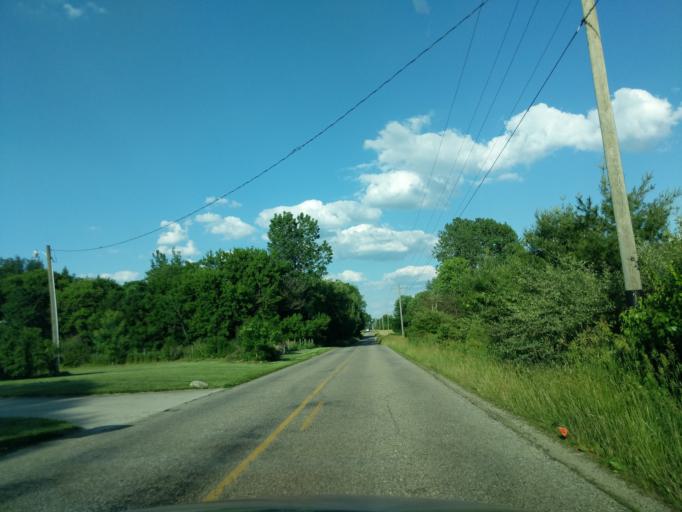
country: US
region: Indiana
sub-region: Whitley County
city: Tri-Lakes
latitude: 41.3021
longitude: -85.5156
